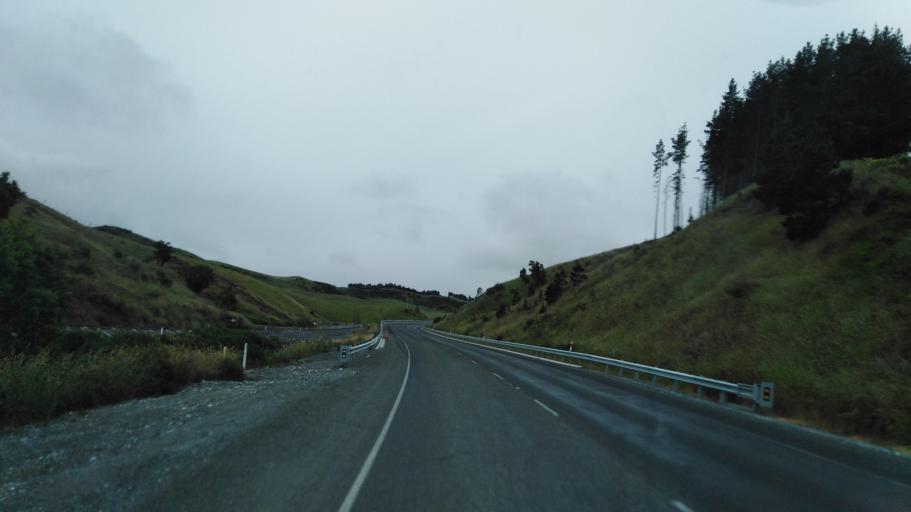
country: NZ
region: Marlborough
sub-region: Marlborough District
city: Blenheim
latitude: -41.8942
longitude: 174.1165
